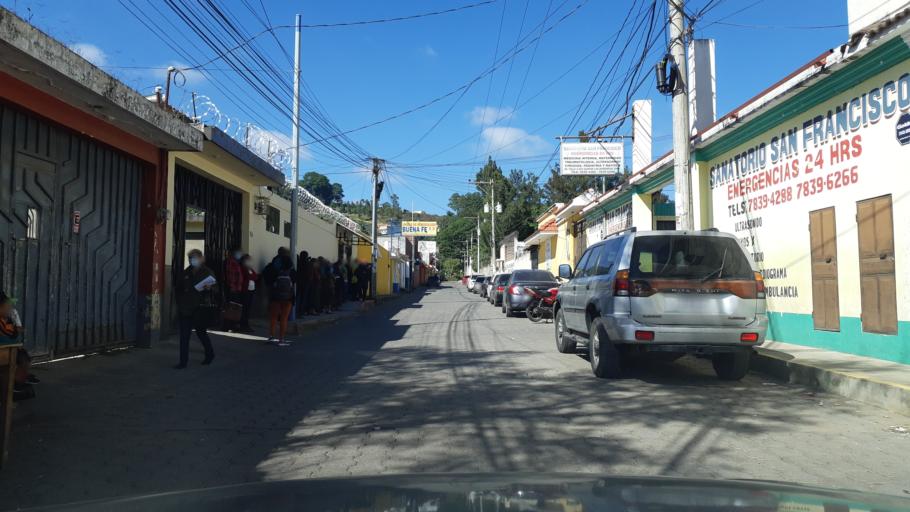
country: GT
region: Chimaltenango
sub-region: Municipio de Chimaltenango
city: Chimaltenango
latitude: 14.6526
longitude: -90.8163
